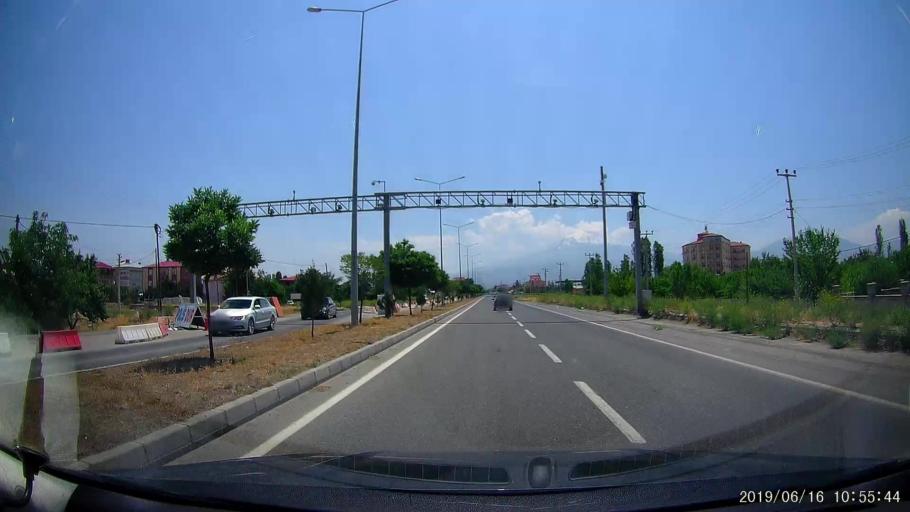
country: TR
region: Igdir
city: Igdir
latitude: 39.9348
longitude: 44.0134
